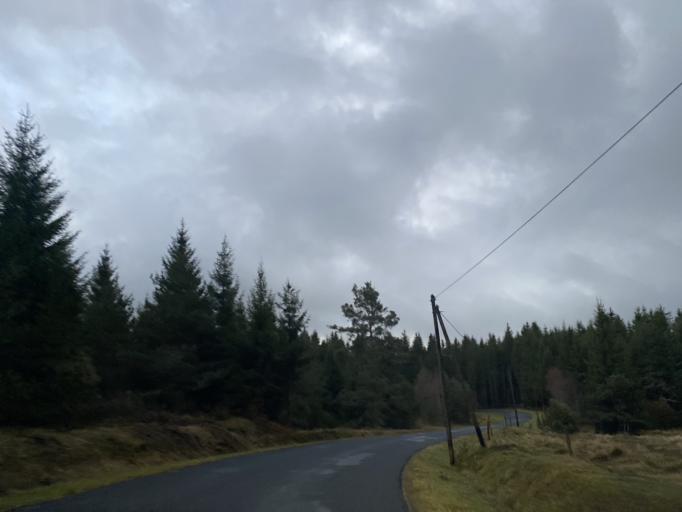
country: FR
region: Auvergne
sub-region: Departement du Puy-de-Dome
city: Cunlhat
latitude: 45.5376
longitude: 3.5813
